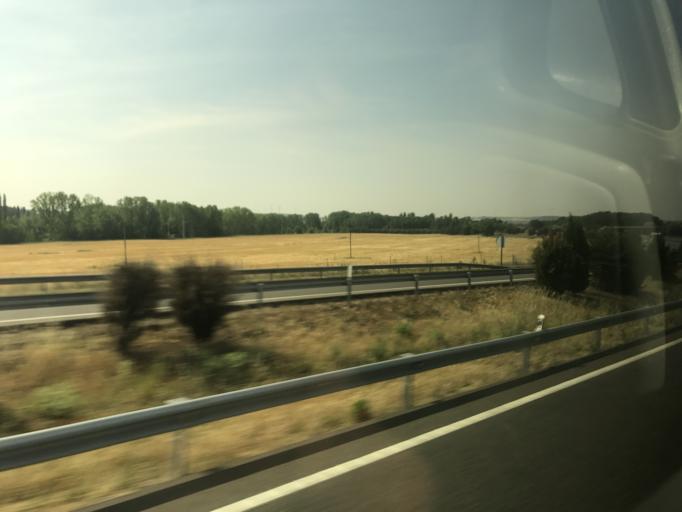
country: ES
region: Castille and Leon
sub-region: Provincia de Palencia
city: Quintana del Puente
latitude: 42.0938
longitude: -4.2074
